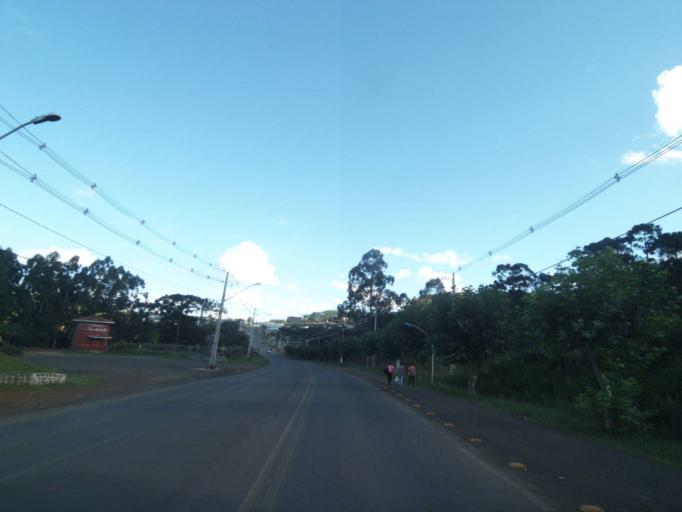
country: BR
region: Parana
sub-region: Uniao Da Vitoria
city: Uniao da Vitoria
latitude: -26.1575
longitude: -51.5414
